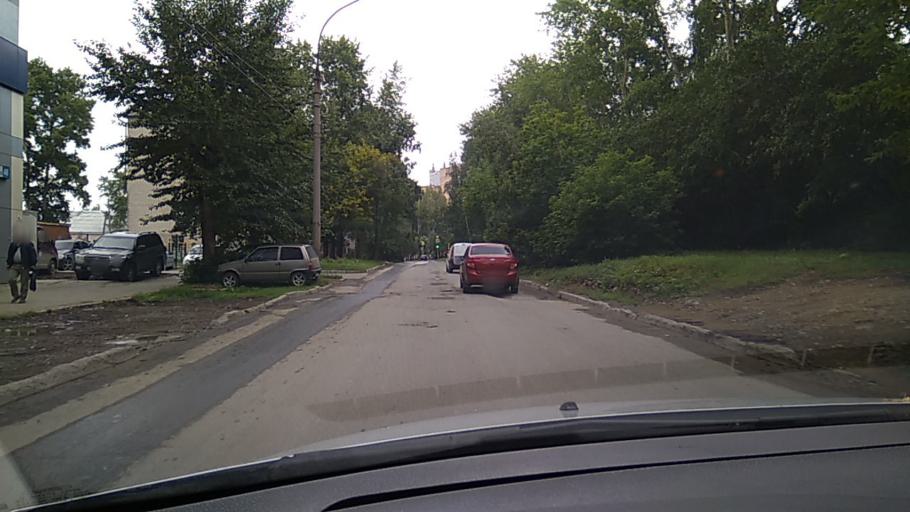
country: RU
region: Sverdlovsk
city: Sovkhoznyy
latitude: 56.7662
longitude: 60.6078
